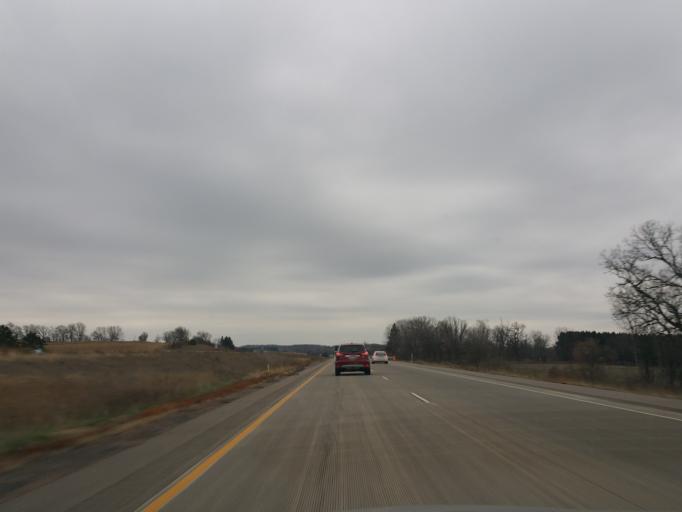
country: US
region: Wisconsin
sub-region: Eau Claire County
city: Fall Creek
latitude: 44.6547
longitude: -91.3123
